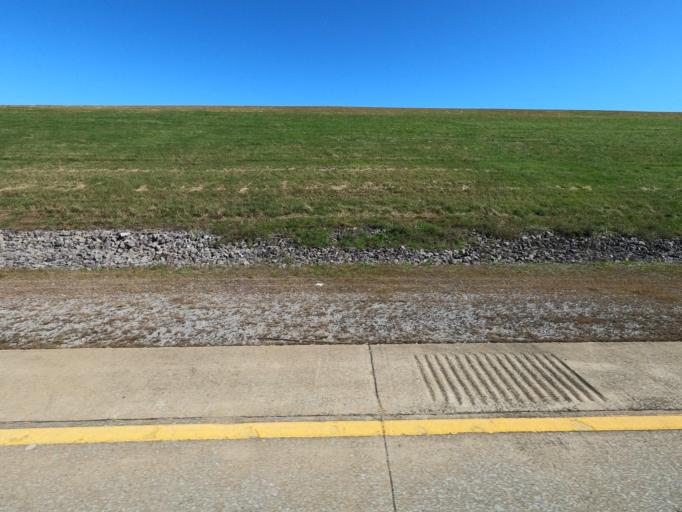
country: US
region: Tennessee
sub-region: Williamson County
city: Fairview
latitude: 35.9378
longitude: -87.1905
